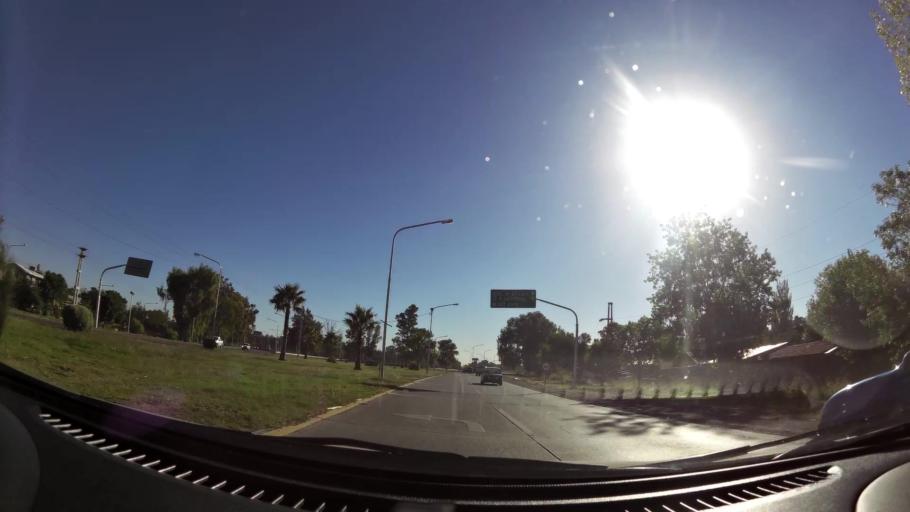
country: AR
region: Mendoza
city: Las Heras
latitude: -32.8484
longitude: -68.8031
